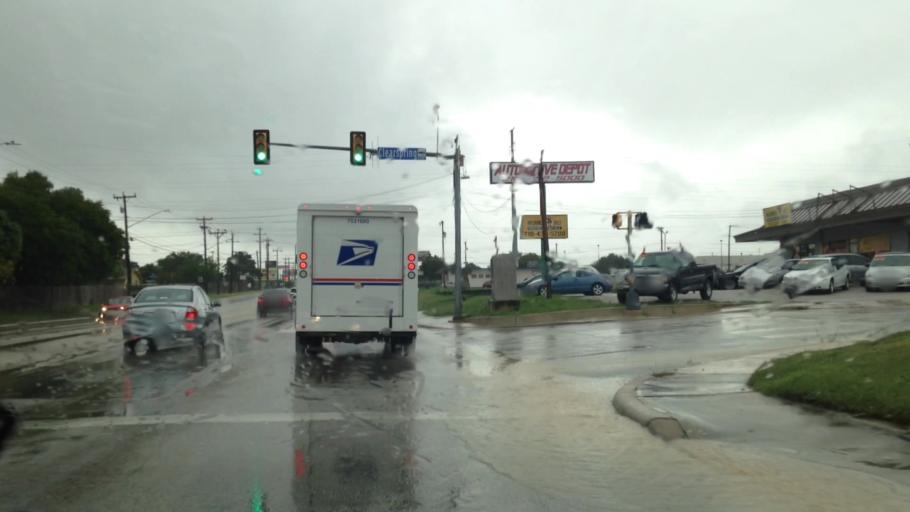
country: US
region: Texas
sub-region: Bexar County
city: Windcrest
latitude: 29.5289
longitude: -98.4110
